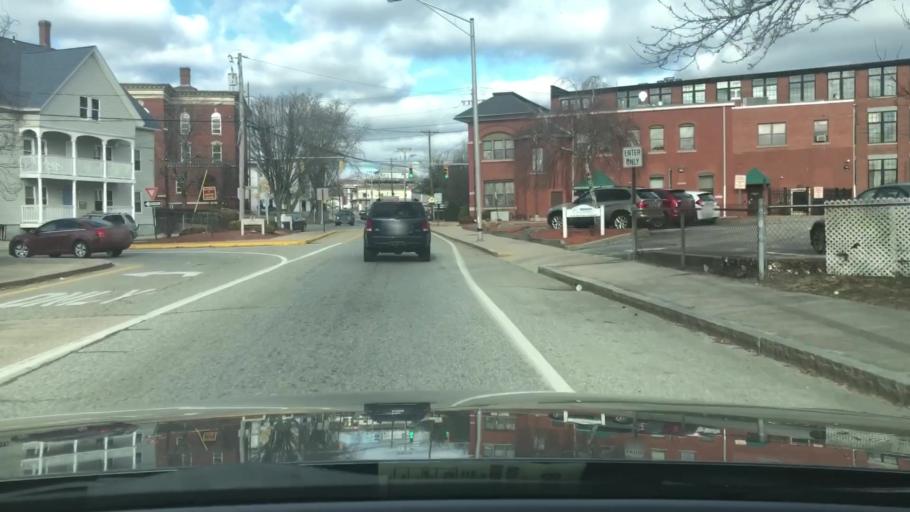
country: US
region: Rhode Island
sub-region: Providence County
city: Woonsocket
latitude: 42.0095
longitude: -71.5021
